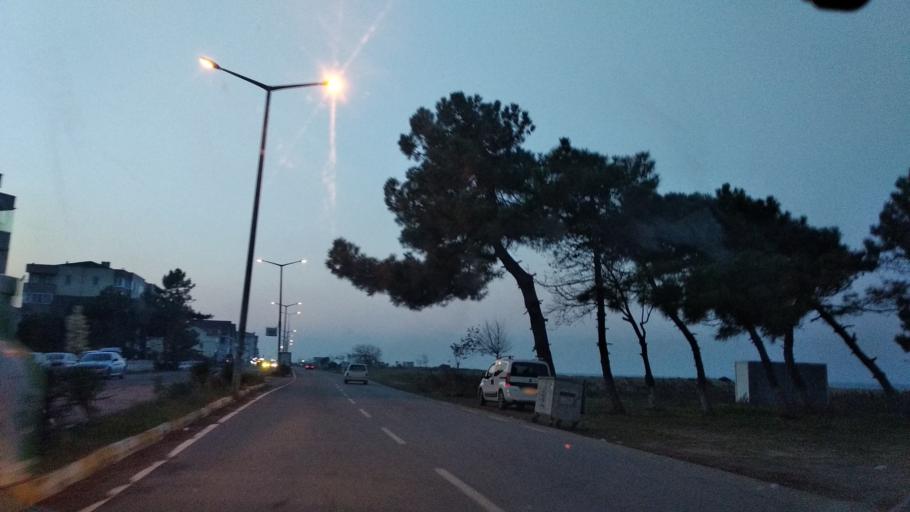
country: TR
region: Sakarya
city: Karasu
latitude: 41.0955
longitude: 30.7319
